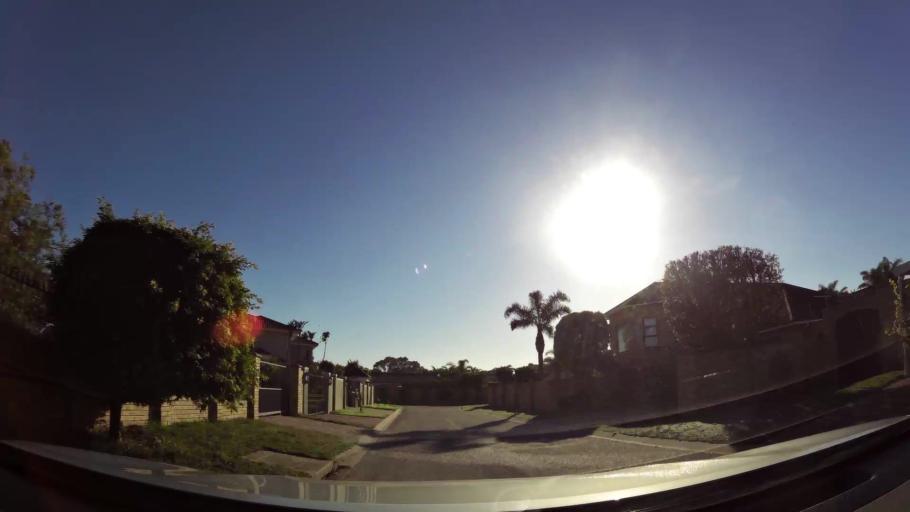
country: ZA
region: Eastern Cape
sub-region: Nelson Mandela Bay Metropolitan Municipality
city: Port Elizabeth
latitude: -33.9876
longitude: 25.6502
